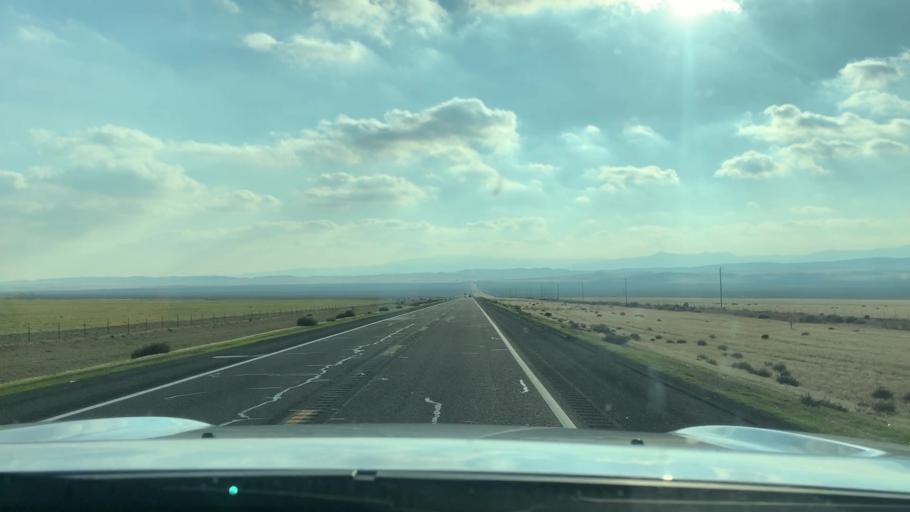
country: US
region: California
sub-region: Kings County
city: Kettleman City
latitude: 35.9268
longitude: -120.0228
